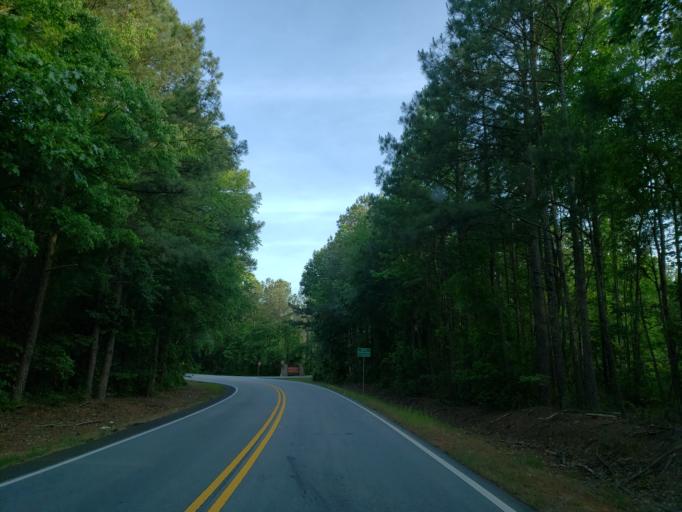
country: US
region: Georgia
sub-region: Carroll County
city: Mount Zion
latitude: 33.6125
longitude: -85.1694
